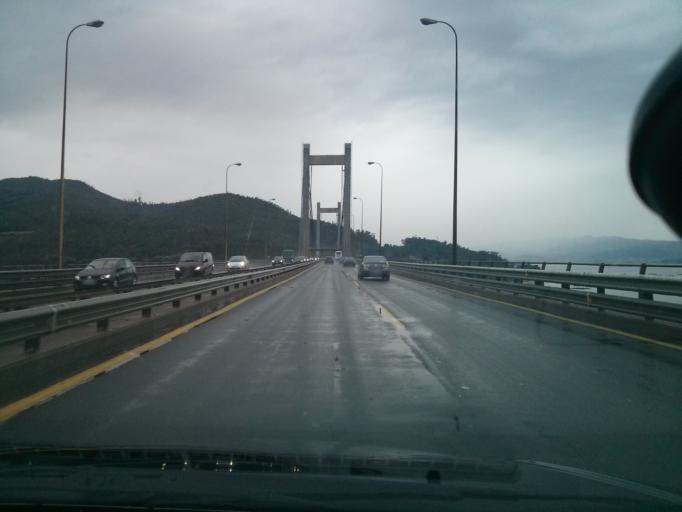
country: ES
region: Galicia
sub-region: Provincia de Pontevedra
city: Redondela
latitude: 42.2825
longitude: -8.6612
